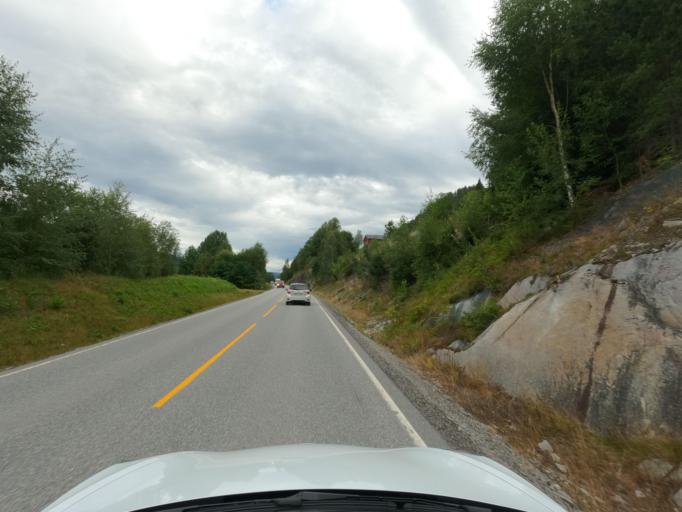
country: NO
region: Telemark
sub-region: Hjartdal
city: Sauland
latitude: 59.7507
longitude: 9.0186
